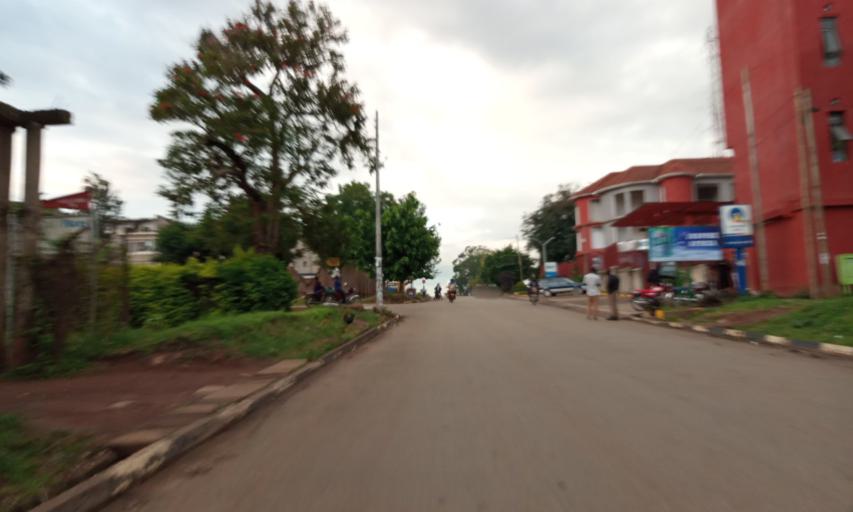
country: UG
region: Eastern Region
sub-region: Mbale District
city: Mbale
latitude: 1.0703
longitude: 34.1815
